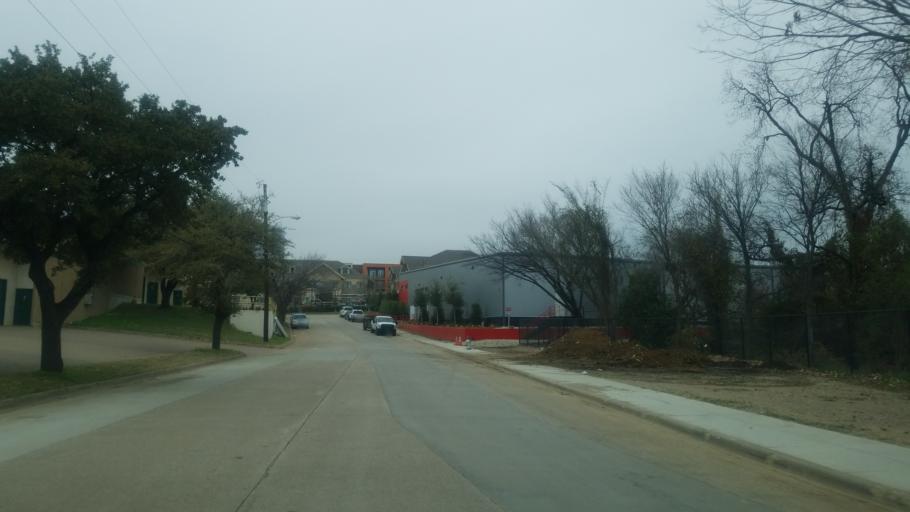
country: US
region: Texas
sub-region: Dallas County
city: Dallas
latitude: 32.8087
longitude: -96.8292
